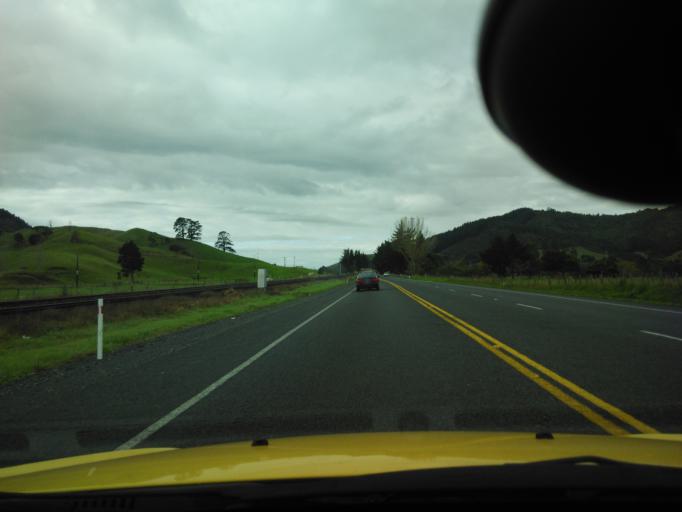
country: NZ
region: Waikato
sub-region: Waikato District
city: Ngaruawahia
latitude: -37.5949
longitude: 175.1610
